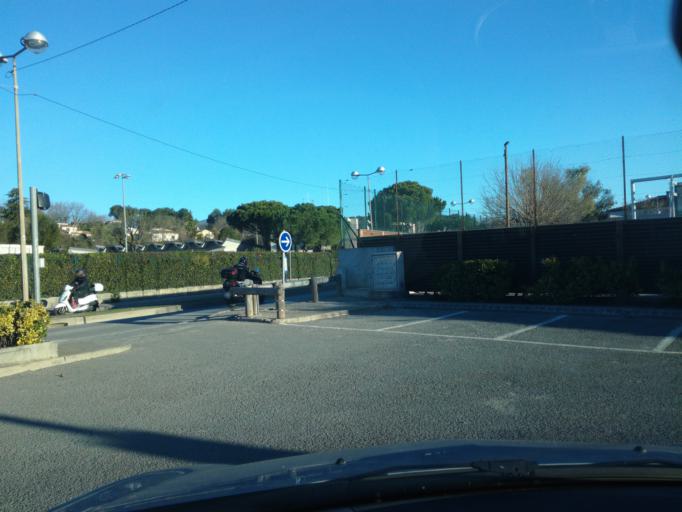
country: FR
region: Provence-Alpes-Cote d'Azur
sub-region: Departement des Alpes-Maritimes
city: La Roquette-sur-Siagne
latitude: 43.6050
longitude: 6.9716
